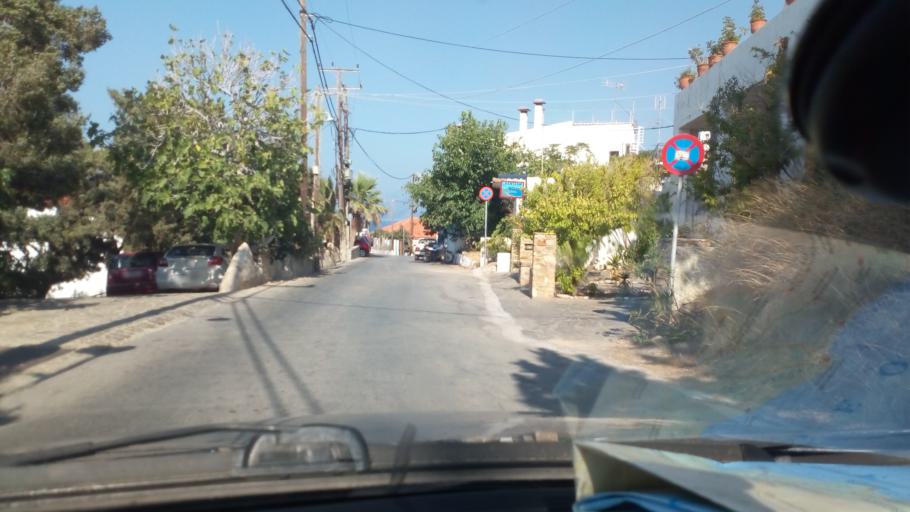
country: GR
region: North Aegean
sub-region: Nomos Samou
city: Agios Kirykos
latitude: 37.6349
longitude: 26.0866
